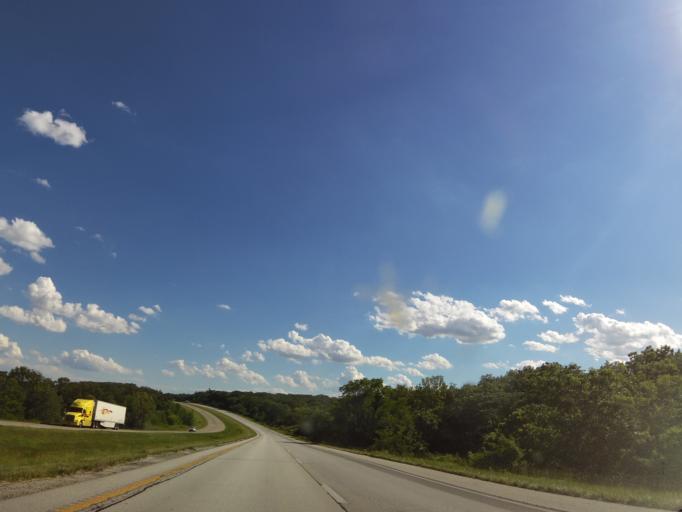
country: US
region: Missouri
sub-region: Lewis County
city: Canton
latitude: 40.1551
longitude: -91.5361
